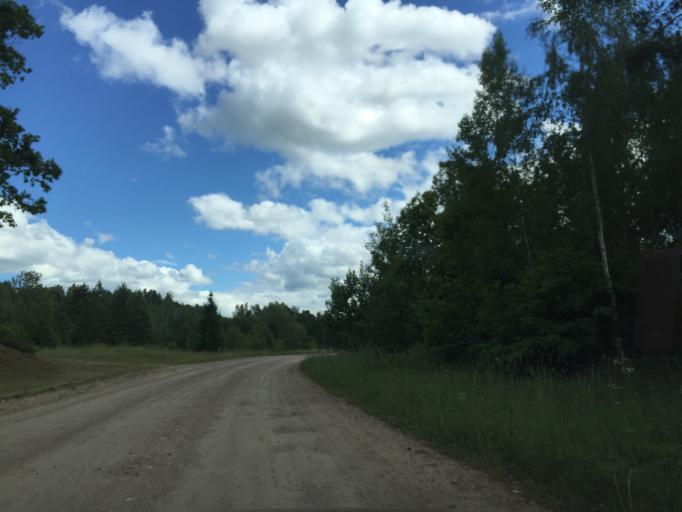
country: LV
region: Vecumnieki
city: Vecumnieki
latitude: 56.5033
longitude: 24.4043
